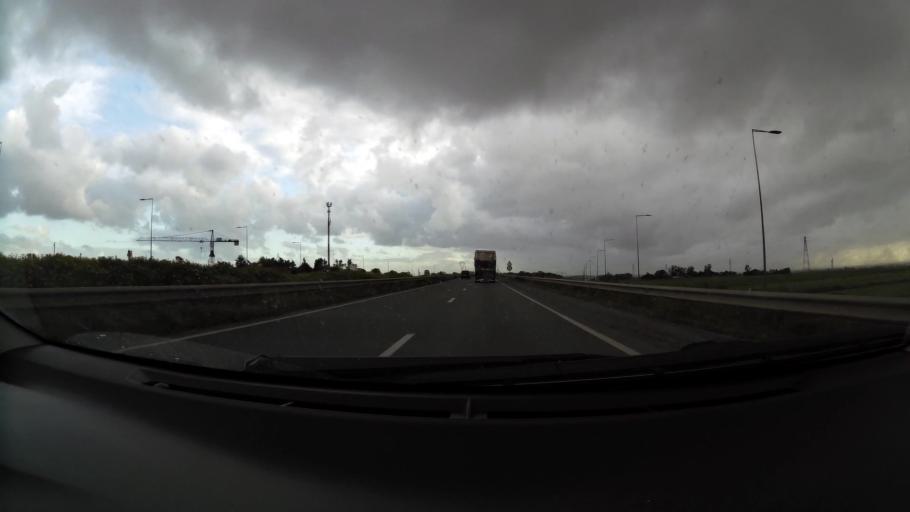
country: MA
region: Grand Casablanca
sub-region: Mohammedia
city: Mohammedia
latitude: 33.6506
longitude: -7.4173
